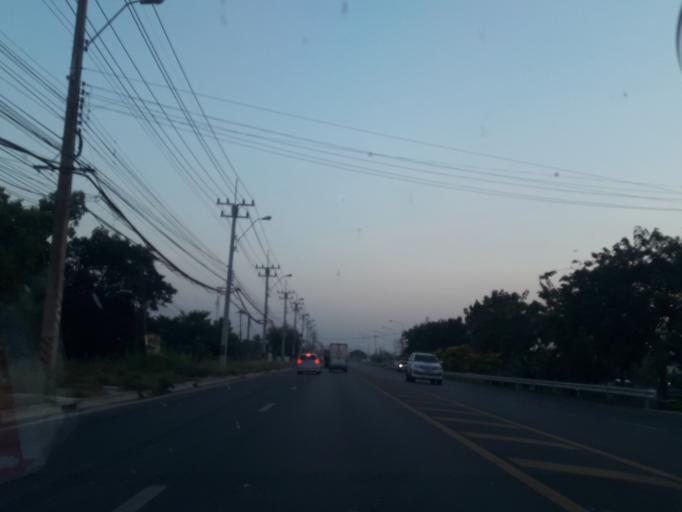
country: TH
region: Pathum Thani
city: Thanyaburi
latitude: 14.0747
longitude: 100.7104
